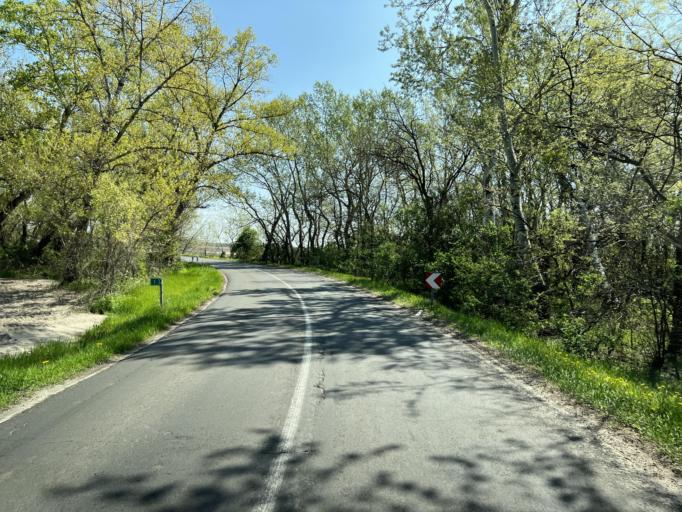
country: HU
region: Pest
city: Alsonemedi
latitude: 47.3013
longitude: 19.1876
